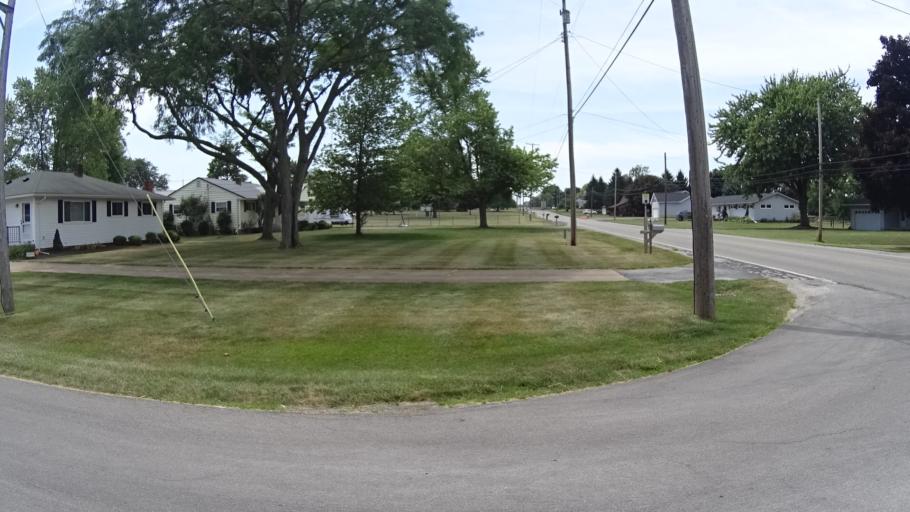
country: US
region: Ohio
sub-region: Erie County
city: Sandusky
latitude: 41.3982
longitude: -82.7846
